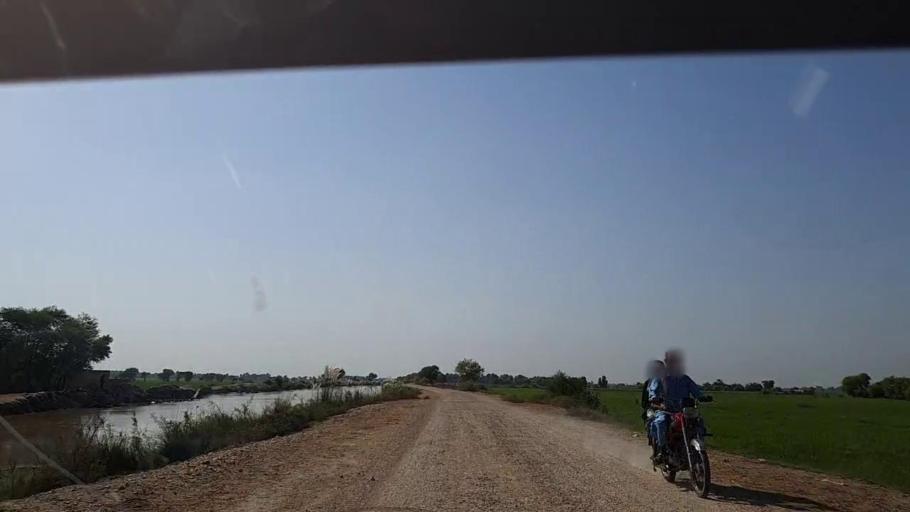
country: PK
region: Sindh
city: Ghauspur
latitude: 28.1861
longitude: 69.0680
